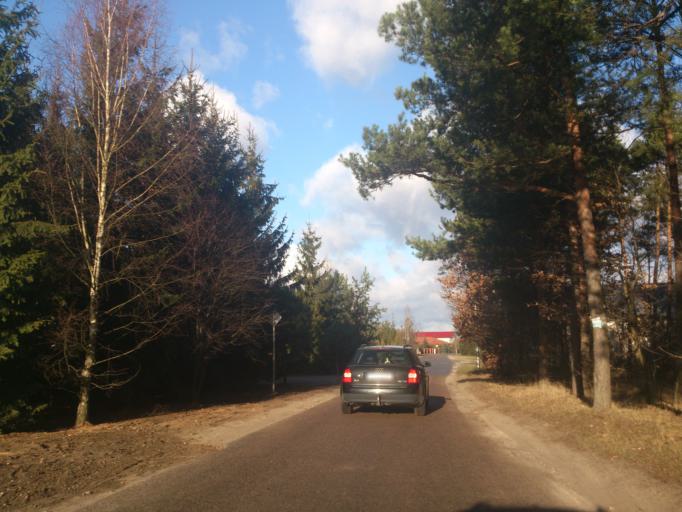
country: PL
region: Kujawsko-Pomorskie
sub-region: Powiat torunski
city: Lubicz Gorny
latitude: 53.0171
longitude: 18.7995
